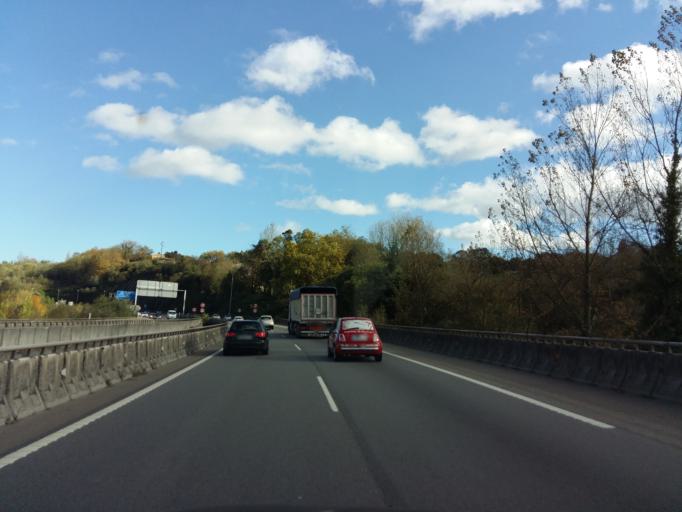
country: ES
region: Asturias
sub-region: Province of Asturias
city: Oviedo
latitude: 43.3485
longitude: -5.8436
